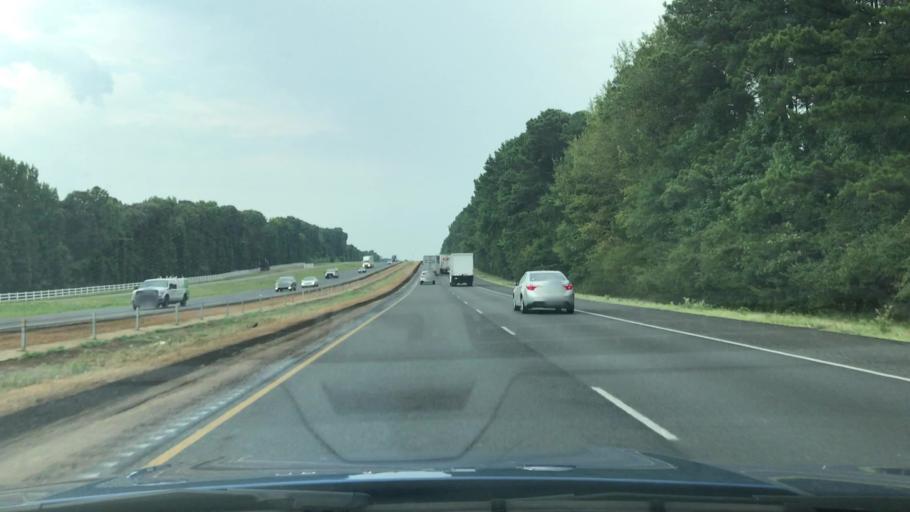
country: US
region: Texas
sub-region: Harrison County
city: Marshall
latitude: 32.4951
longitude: -94.2601
